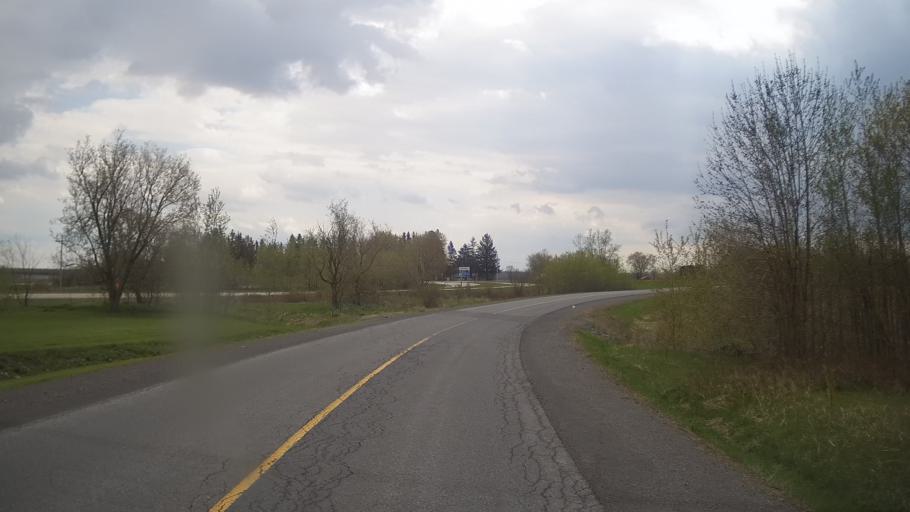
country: CA
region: Ontario
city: Hawkesbury
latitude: 45.5199
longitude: -74.5648
